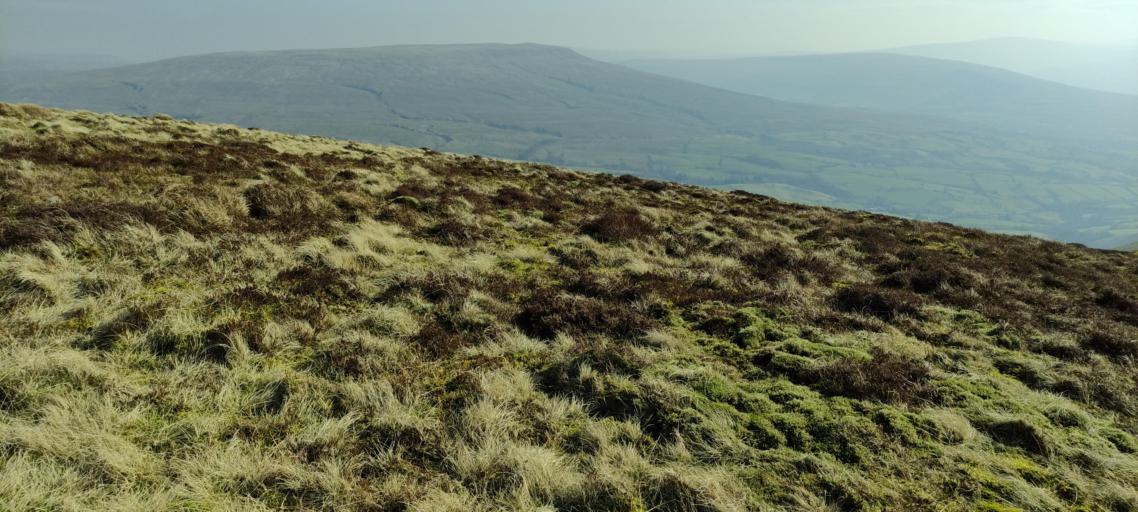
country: GB
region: England
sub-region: Cumbria
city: Sedbergh
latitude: 54.3596
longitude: -2.5010
